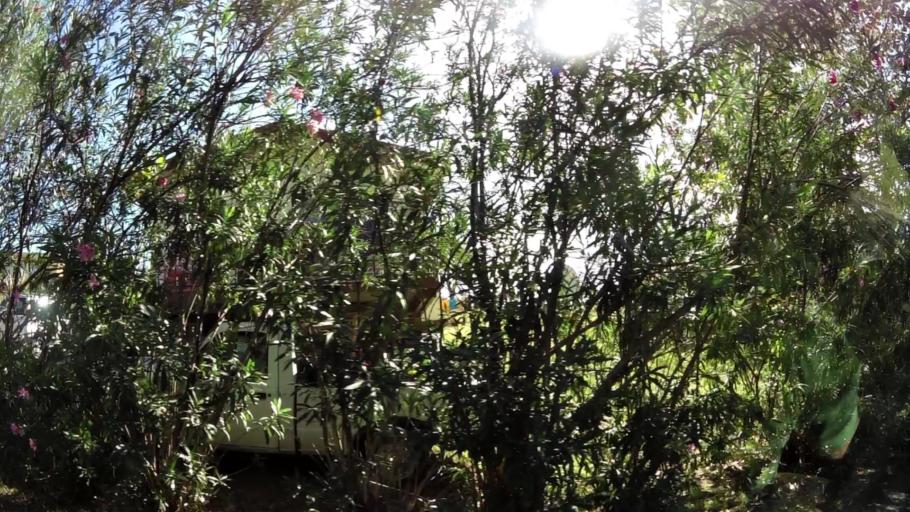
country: VG
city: Tortola
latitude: 18.4900
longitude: -64.3880
